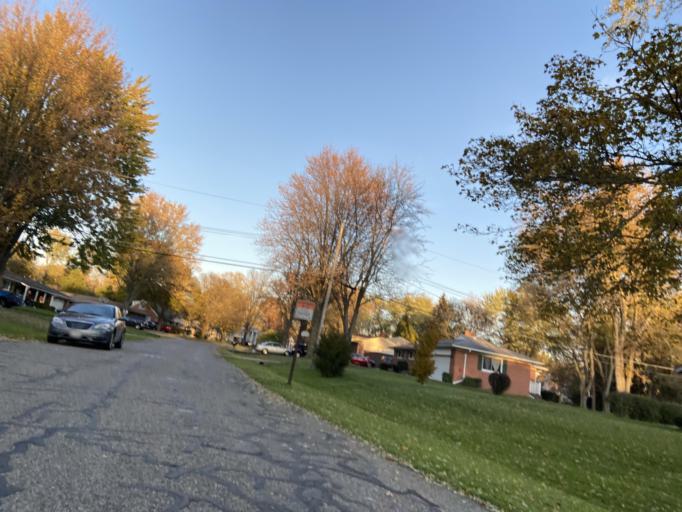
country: US
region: Michigan
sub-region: Oakland County
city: Farmington Hills
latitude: 42.5023
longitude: -83.3698
